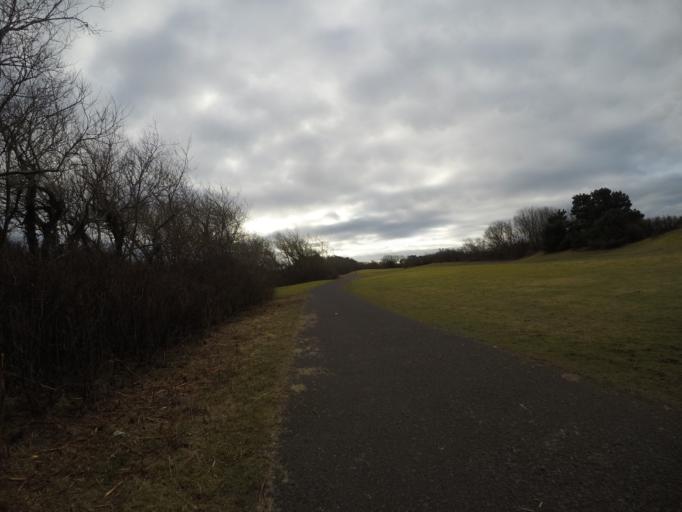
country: GB
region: Scotland
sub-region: North Ayrshire
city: Irvine
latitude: 55.6065
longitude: -4.6825
